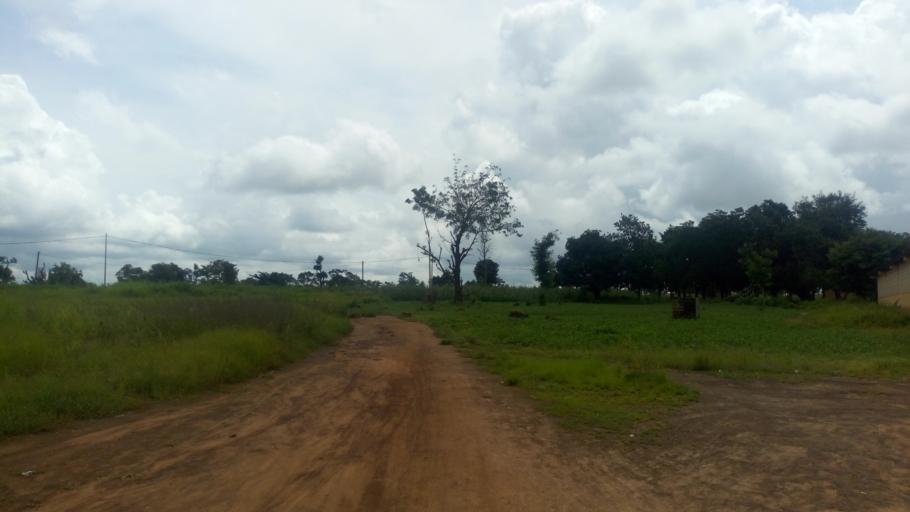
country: TG
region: Centrale
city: Sotouboua
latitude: 8.5568
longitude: 0.9963
